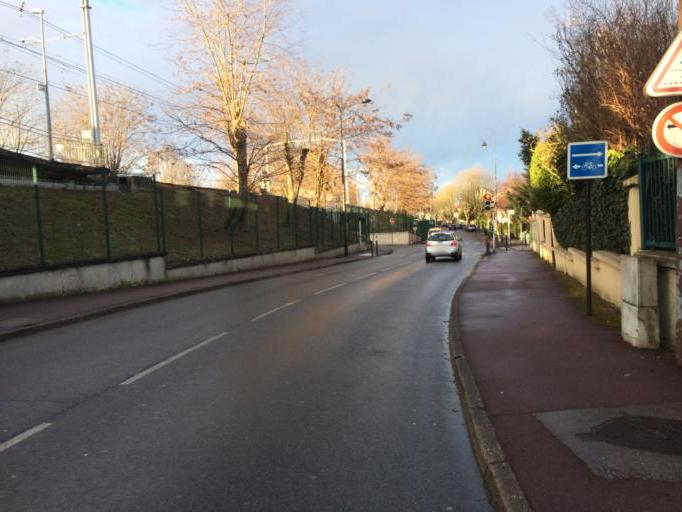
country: FR
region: Ile-de-France
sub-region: Departement des Hauts-de-Seine
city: Antony
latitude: 48.7436
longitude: 2.2970
